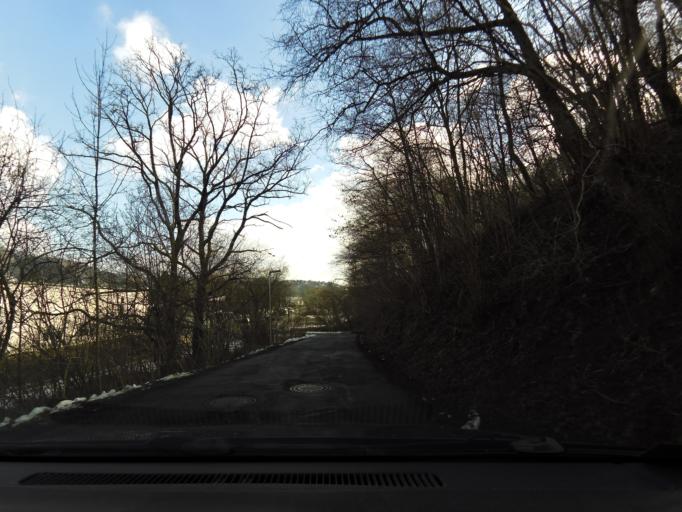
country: DE
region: Lower Saxony
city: Bad Lauterberg im Harz
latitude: 51.6193
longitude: 10.4081
